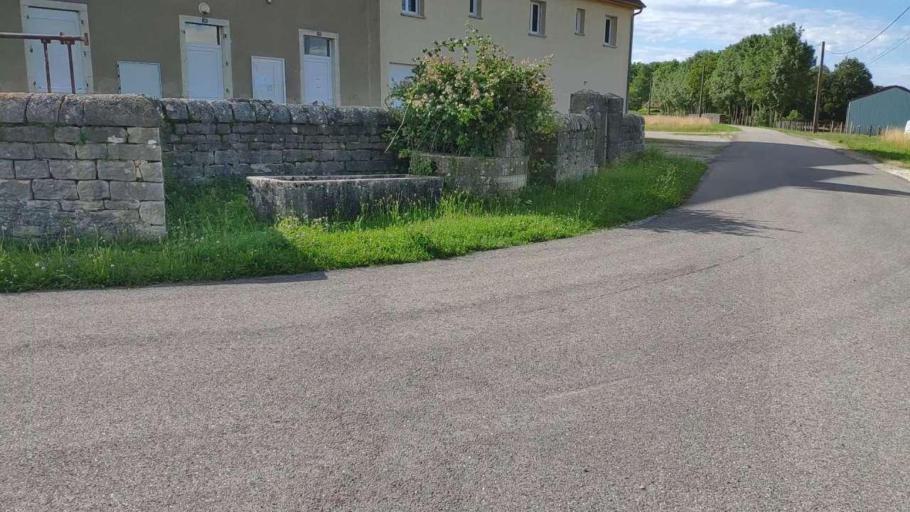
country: FR
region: Franche-Comte
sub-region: Departement du Jura
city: Bletterans
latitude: 46.8087
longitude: 5.5062
